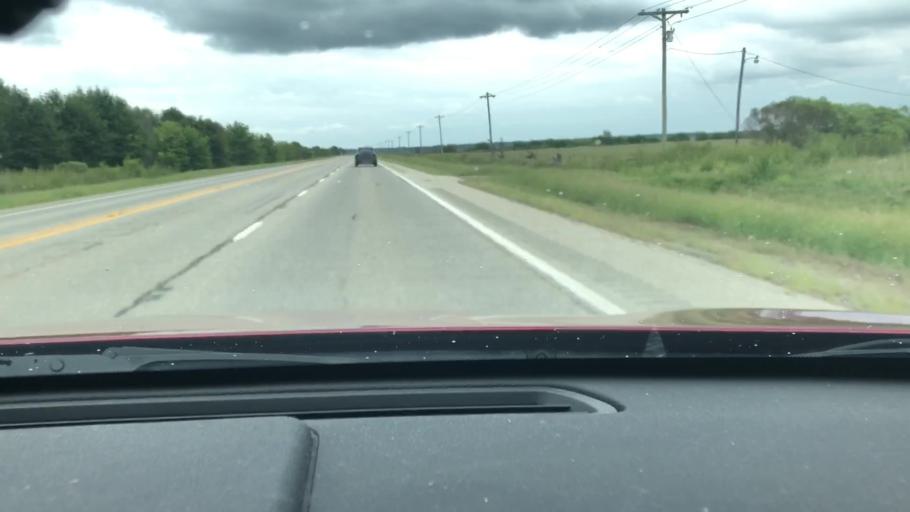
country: US
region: Arkansas
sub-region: Lafayette County
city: Lewisville
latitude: 33.4124
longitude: -93.7907
